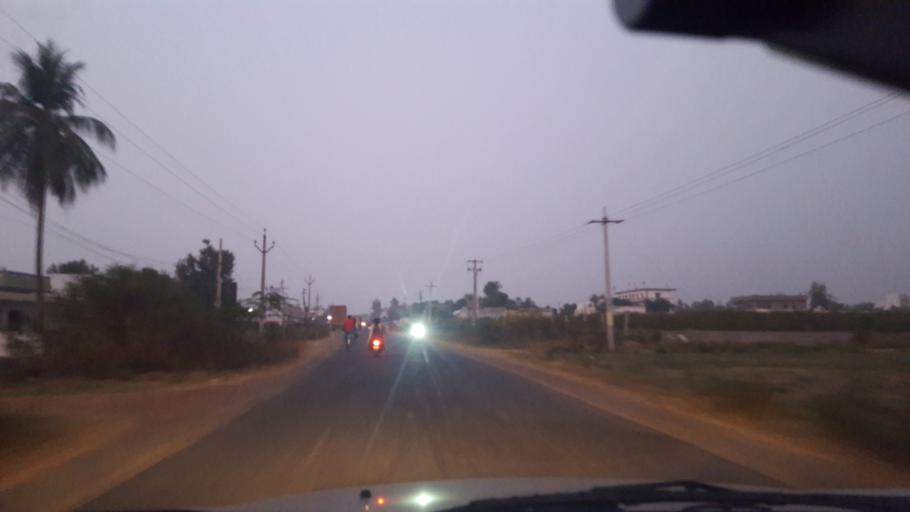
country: IN
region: Andhra Pradesh
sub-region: Srikakulam
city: Palasa
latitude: 18.7452
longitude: 84.4149
